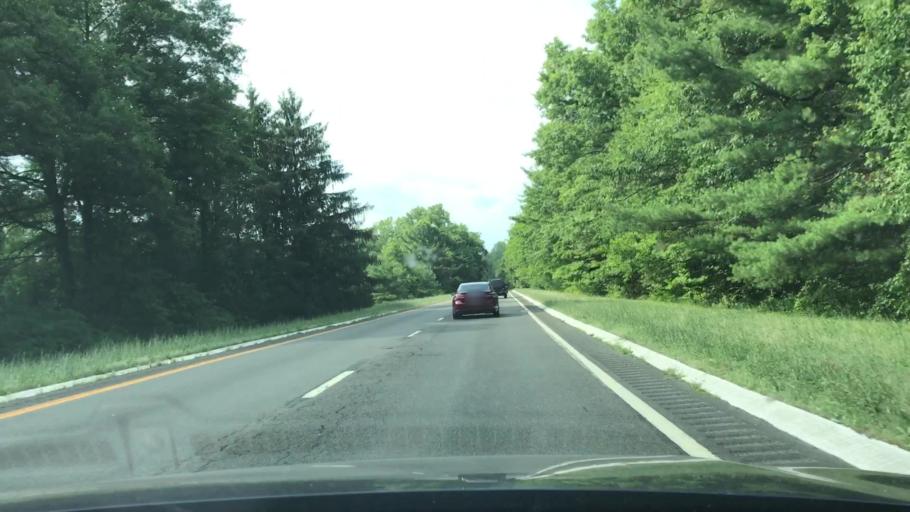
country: US
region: New York
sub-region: Rockland County
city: Bardonia
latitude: 41.1128
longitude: -74.0016
